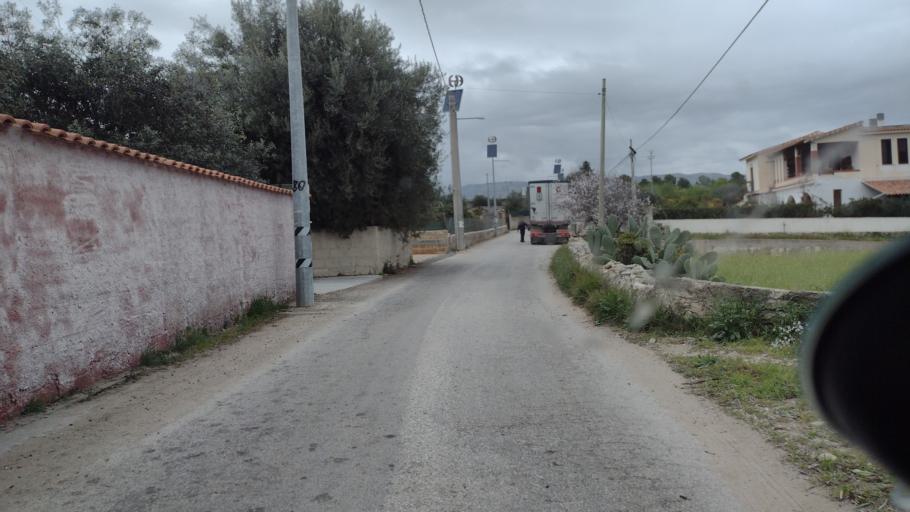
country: IT
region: Sicily
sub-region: Provincia di Siracusa
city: Avola
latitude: 36.8942
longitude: 15.1155
